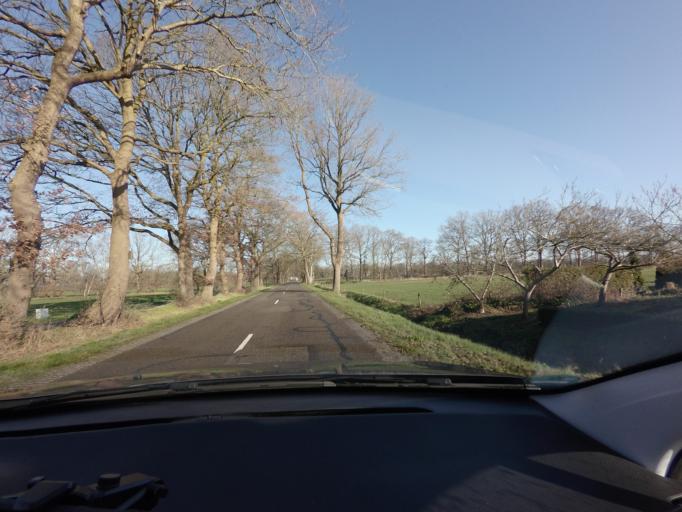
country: NL
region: Drenthe
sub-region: Gemeente Assen
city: Assen
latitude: 52.8652
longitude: 6.5874
